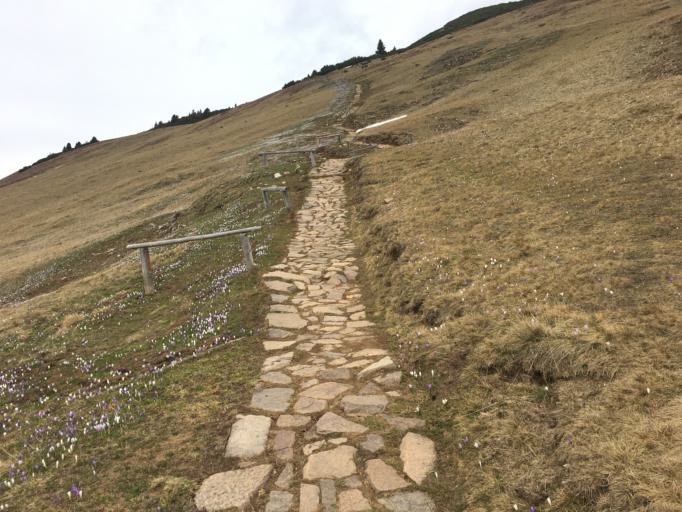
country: IT
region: Trentino-Alto Adige
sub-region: Provincia di Trento
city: Varena
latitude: 46.3481
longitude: 11.4488
